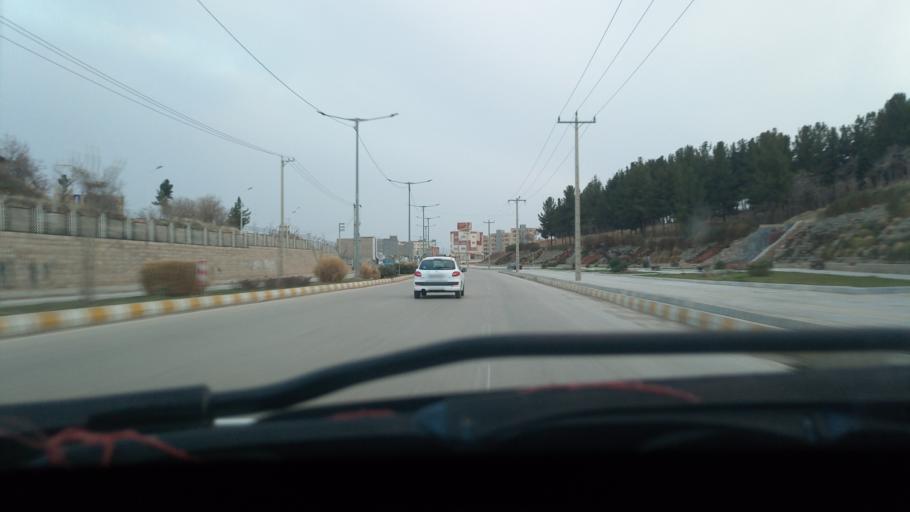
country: IR
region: Khorasan-e Shomali
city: Bojnurd
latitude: 37.4573
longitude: 57.3296
